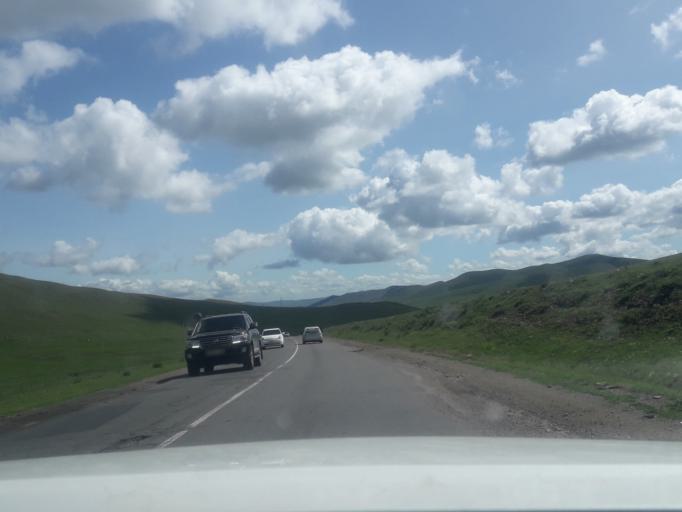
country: MN
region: Central Aimak
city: Ihsueuej
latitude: 48.1257
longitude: 106.4330
